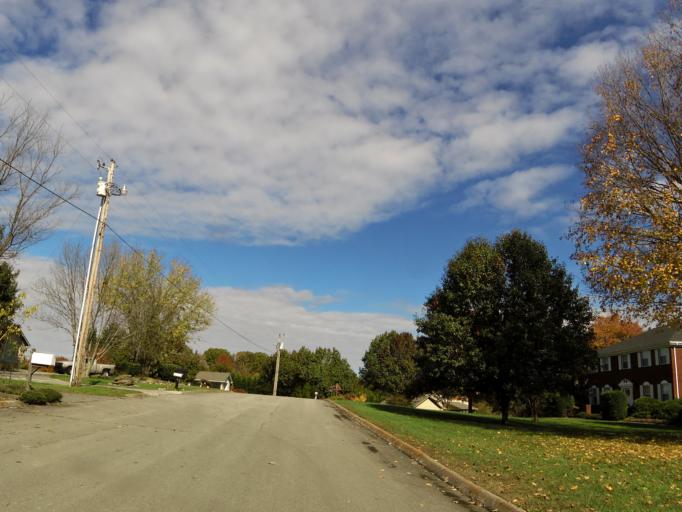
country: US
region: Tennessee
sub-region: Blount County
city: Alcoa
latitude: 35.7738
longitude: -84.0116
